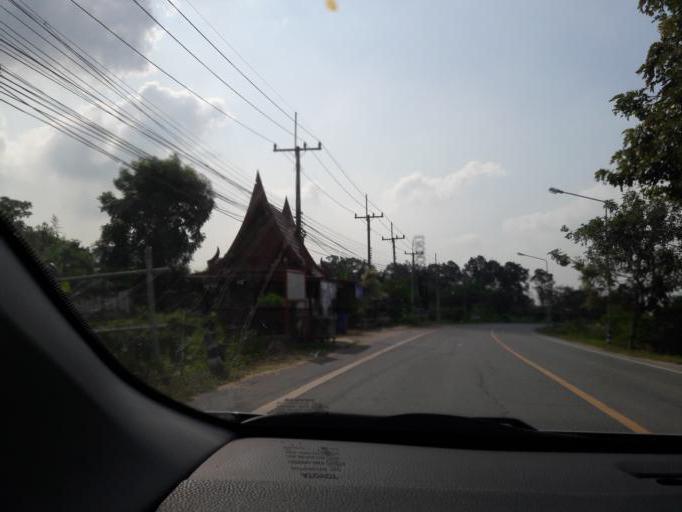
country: TH
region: Ang Thong
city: Ang Thong
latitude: 14.5543
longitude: 100.4436
